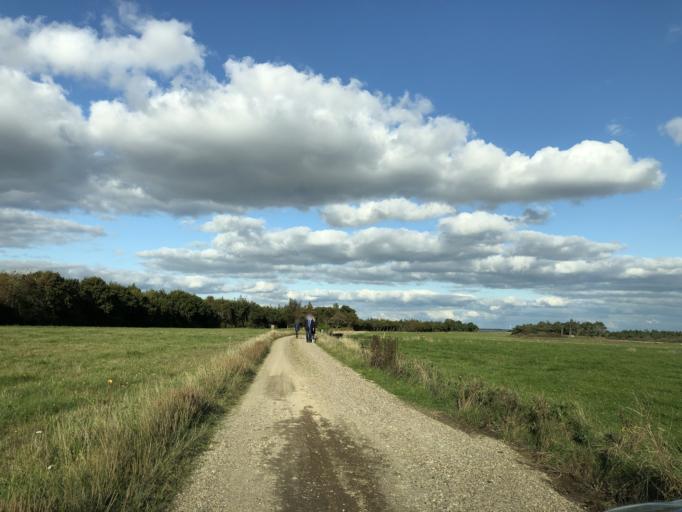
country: DK
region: Central Jutland
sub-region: Holstebro Kommune
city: Ulfborg
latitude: 56.3332
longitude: 8.1612
